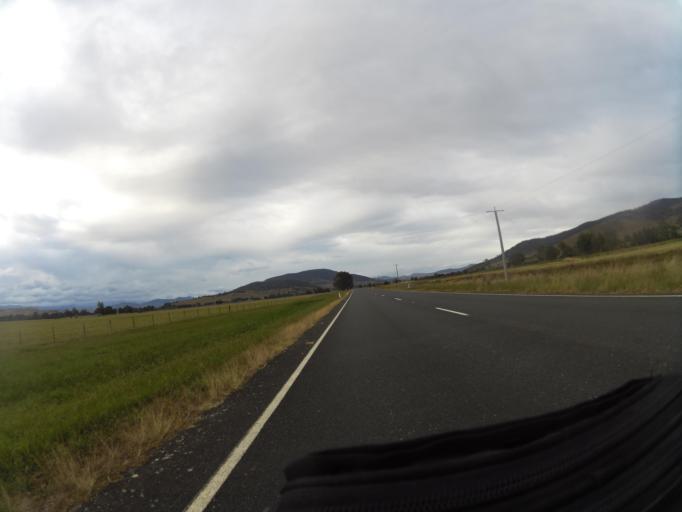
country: AU
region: New South Wales
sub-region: Snowy River
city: Jindabyne
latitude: -36.0997
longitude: 147.9812
